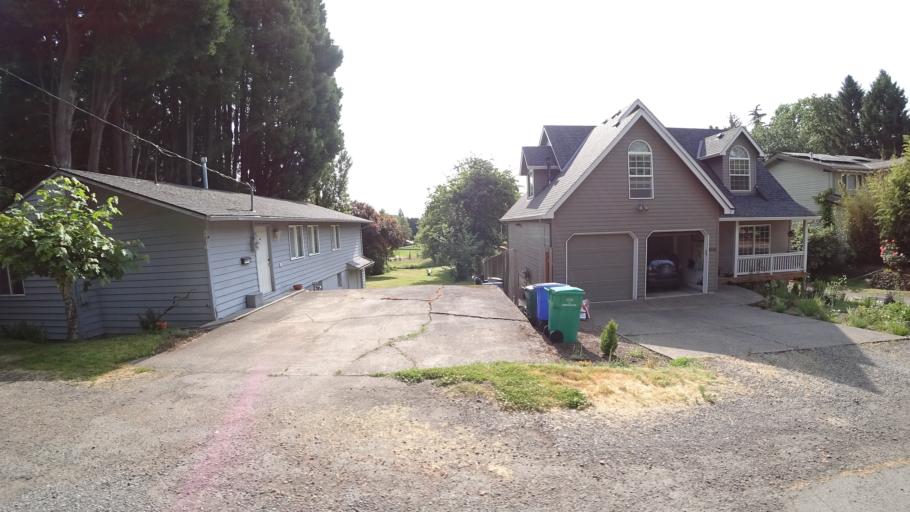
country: US
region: Oregon
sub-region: Washington County
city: Garden Home-Whitford
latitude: 45.4628
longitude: -122.7128
